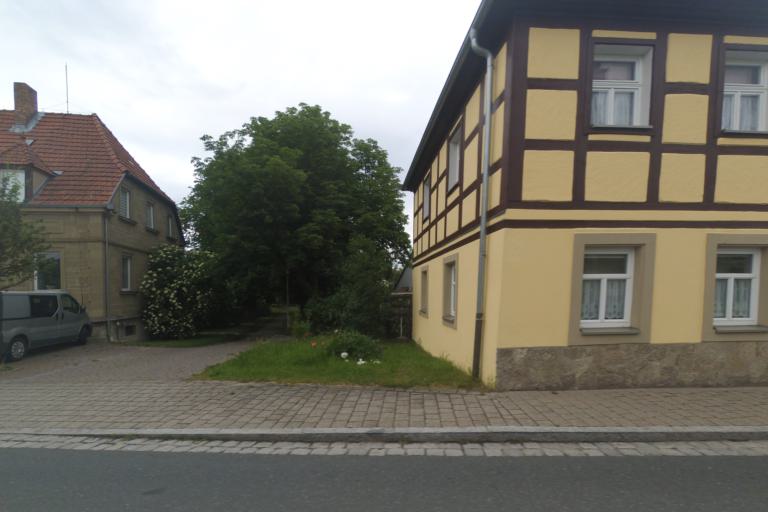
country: DE
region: Bavaria
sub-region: Regierungsbezirk Mittelfranken
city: Langenfeld
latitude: 49.6150
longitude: 10.4790
